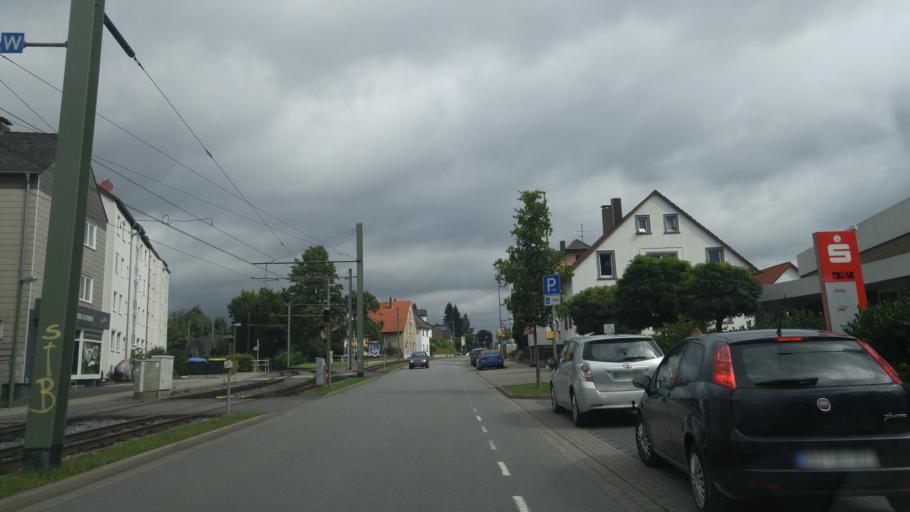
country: DE
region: North Rhine-Westphalia
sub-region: Regierungsbezirk Detmold
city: Bielefeld
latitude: 52.0472
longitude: 8.5444
